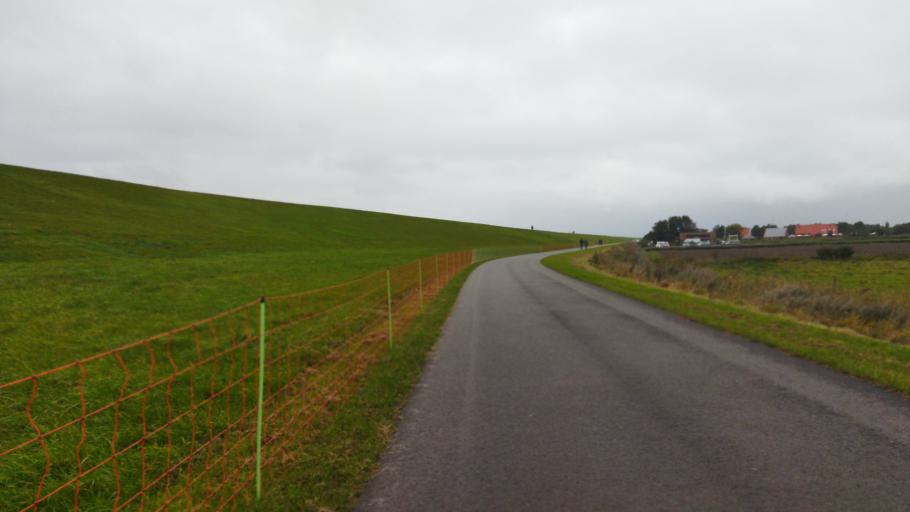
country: NL
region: Groningen
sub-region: Gemeente Delfzijl
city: Delfzijl
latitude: 53.4161
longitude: 7.0136
